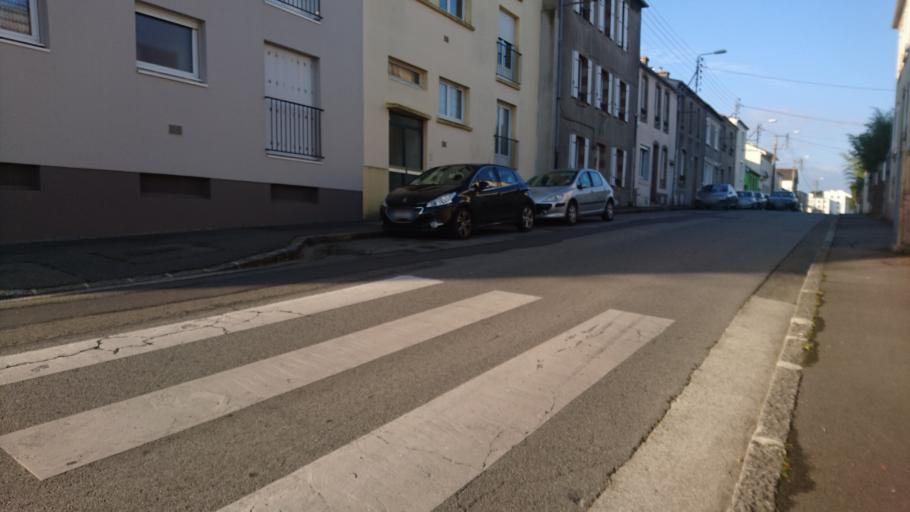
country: FR
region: Brittany
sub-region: Departement du Finistere
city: Brest
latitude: 48.3973
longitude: -4.4548
